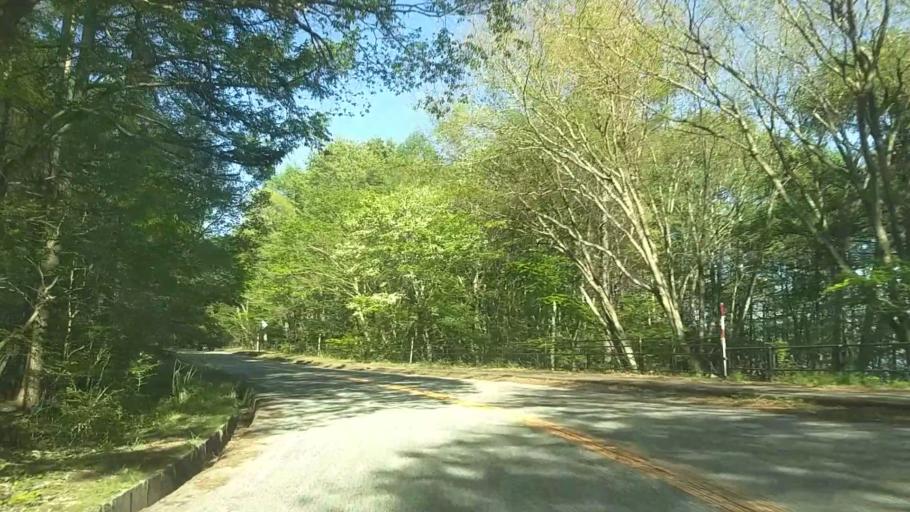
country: JP
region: Yamanashi
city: Nirasaki
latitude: 35.8984
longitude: 138.3657
